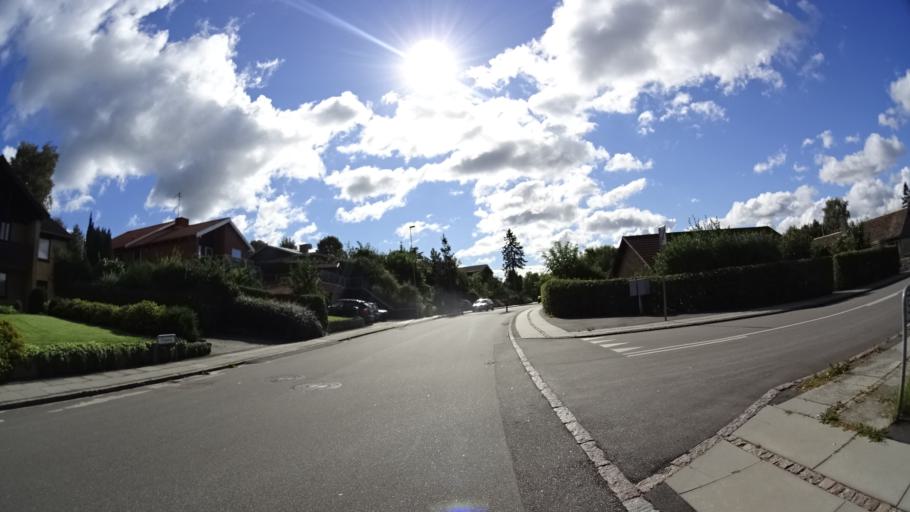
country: DK
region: Central Jutland
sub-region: Arhus Kommune
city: Arhus
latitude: 56.1169
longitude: 10.1836
